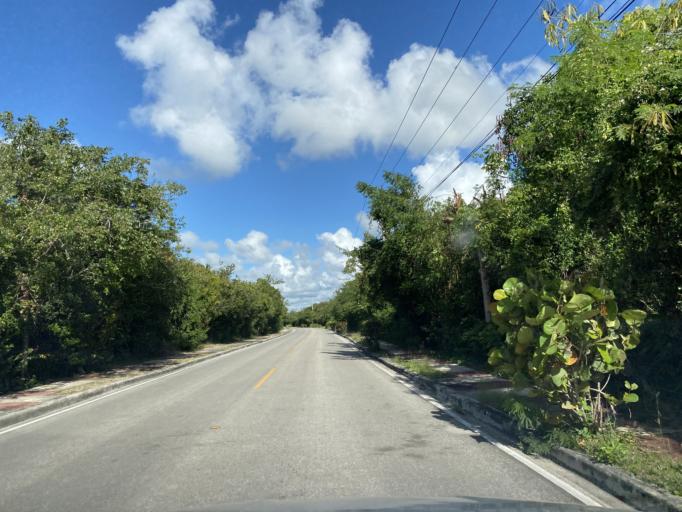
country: DO
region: La Altagracia
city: San Rafael del Yuma
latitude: 18.3402
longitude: -68.8122
